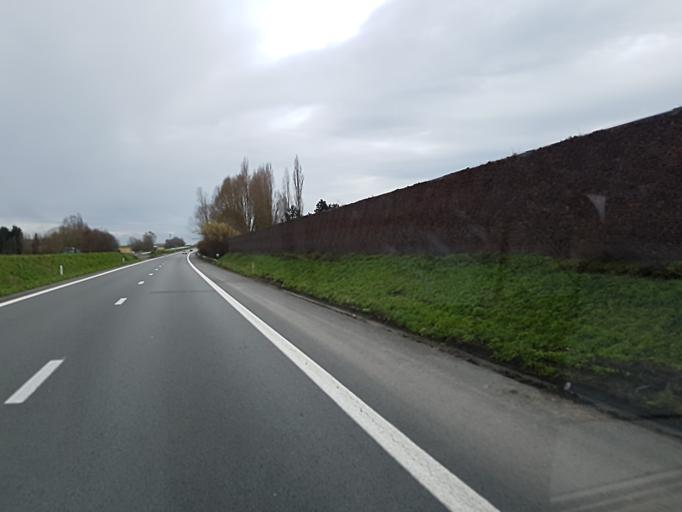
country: BE
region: Flanders
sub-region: Provincie West-Vlaanderen
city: Kortrijk
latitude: 50.7729
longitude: 3.2645
